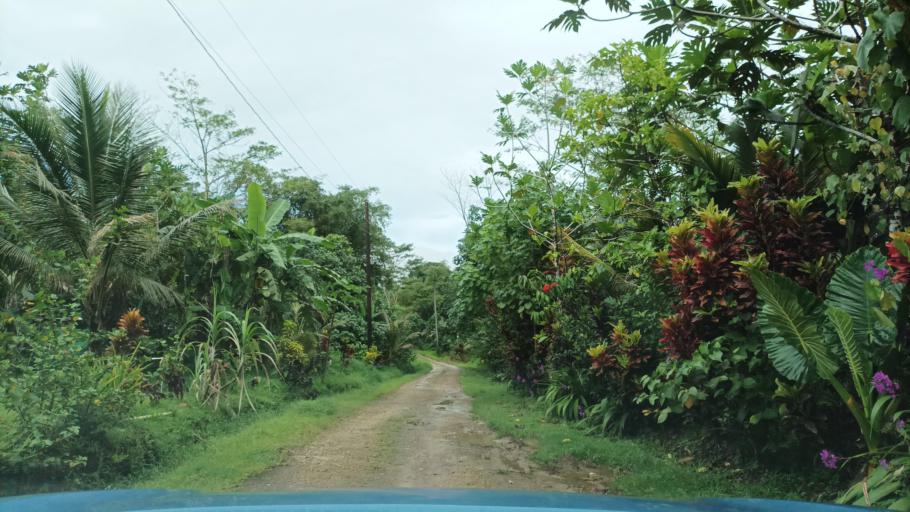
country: FM
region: Pohnpei
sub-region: Sokehs Municipality
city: Palikir - National Government Center
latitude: 6.8537
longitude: 158.1841
